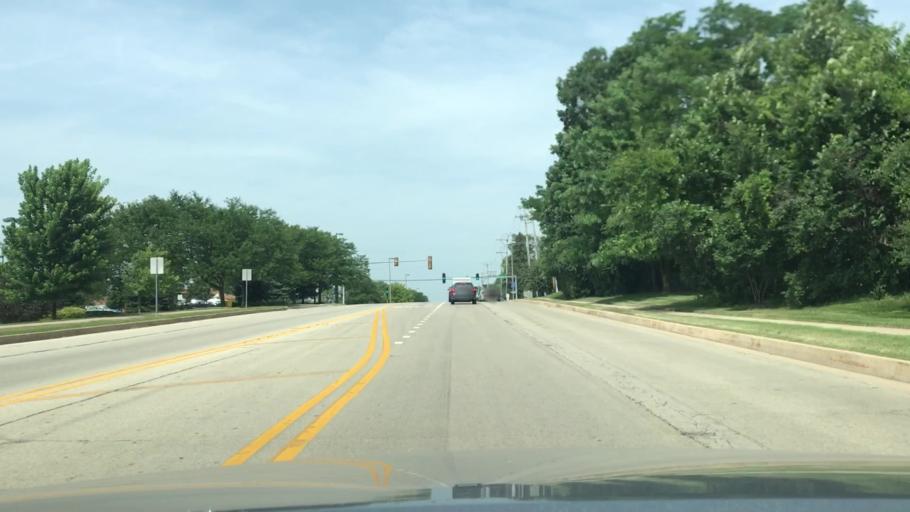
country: US
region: Illinois
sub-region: DuPage County
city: Darien
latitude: 41.7366
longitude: -88.0104
